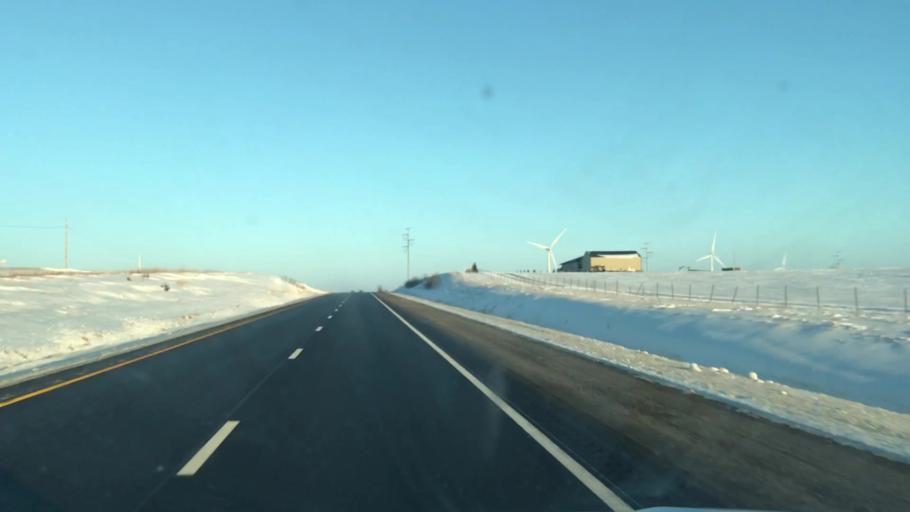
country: US
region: Missouri
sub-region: DeKalb County
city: Maysville
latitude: 39.7618
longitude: -94.4502
